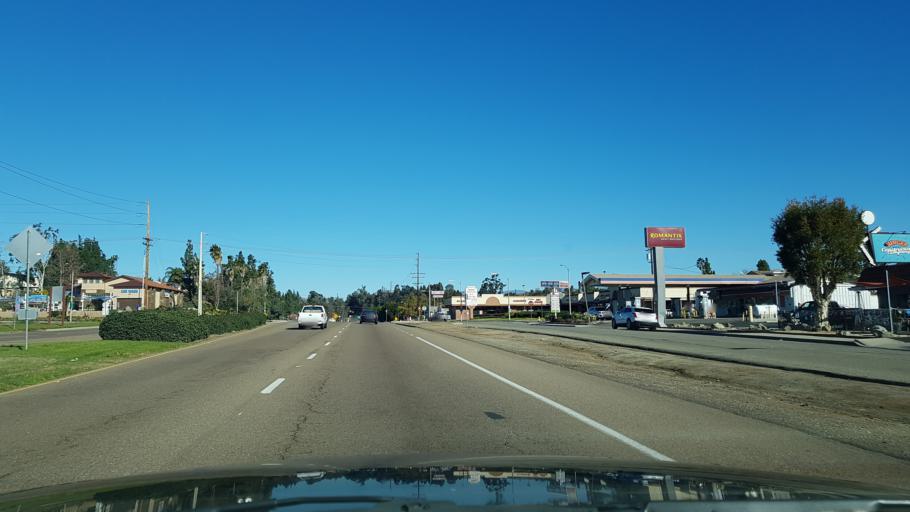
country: US
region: California
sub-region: San Diego County
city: Escondido
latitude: 33.0929
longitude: -117.0721
